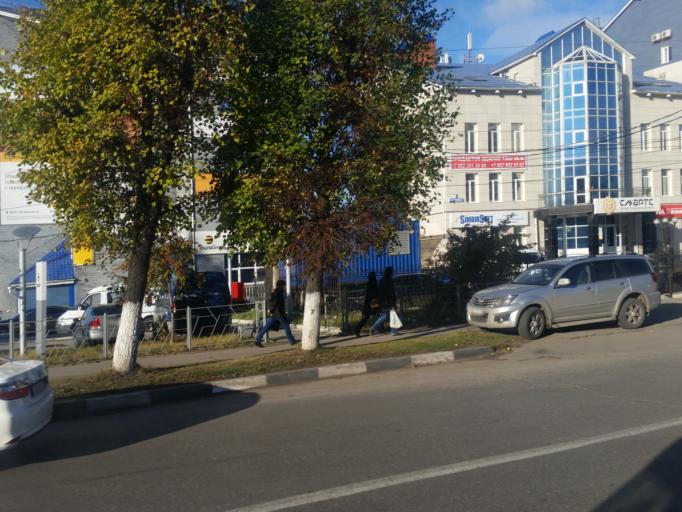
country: RU
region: Ulyanovsk
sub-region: Ulyanovskiy Rayon
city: Ulyanovsk
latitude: 54.3334
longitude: 48.3851
